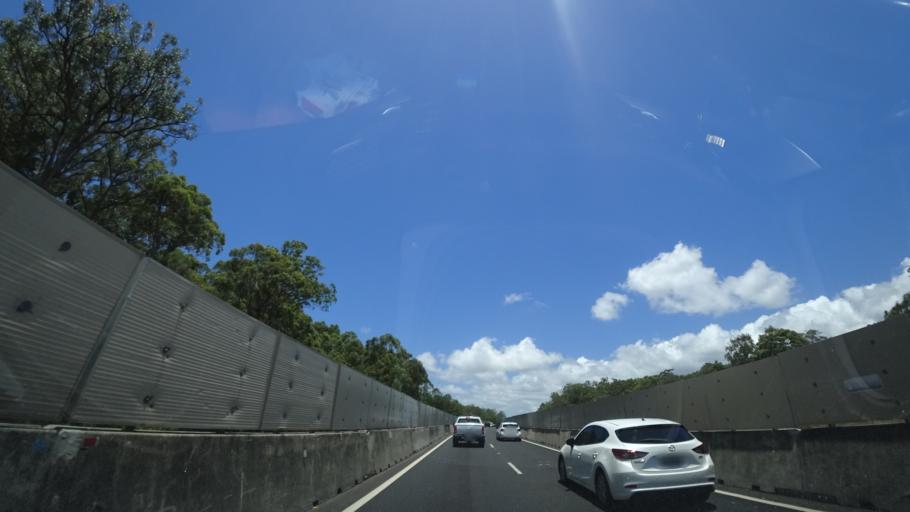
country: AU
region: Queensland
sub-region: Sunshine Coast
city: Little Mountain
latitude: -26.7832
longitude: 153.0449
